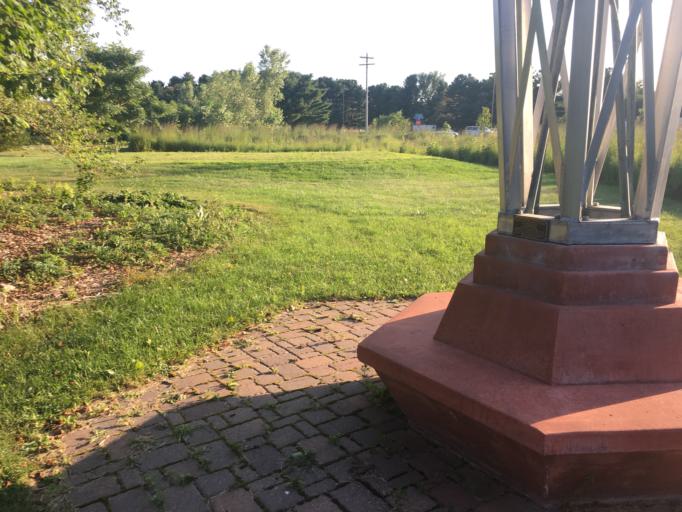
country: US
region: Minnesota
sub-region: Olmsted County
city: Rochester
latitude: 44.0198
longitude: -92.4381
